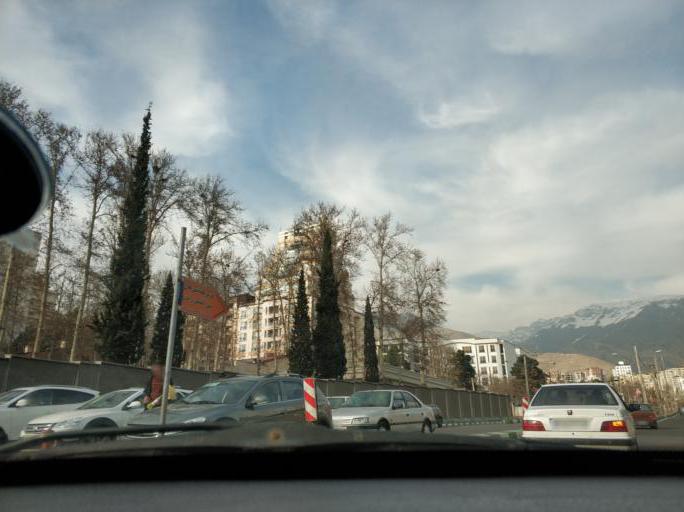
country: IR
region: Tehran
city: Tajrish
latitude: 35.8012
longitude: 51.4806
